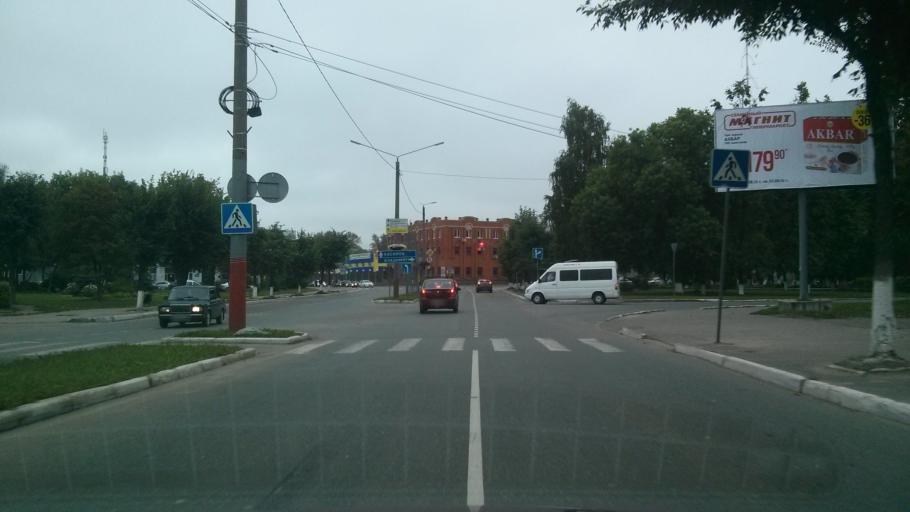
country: RU
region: Vladimir
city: Murom
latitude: 55.5766
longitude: 42.0353
